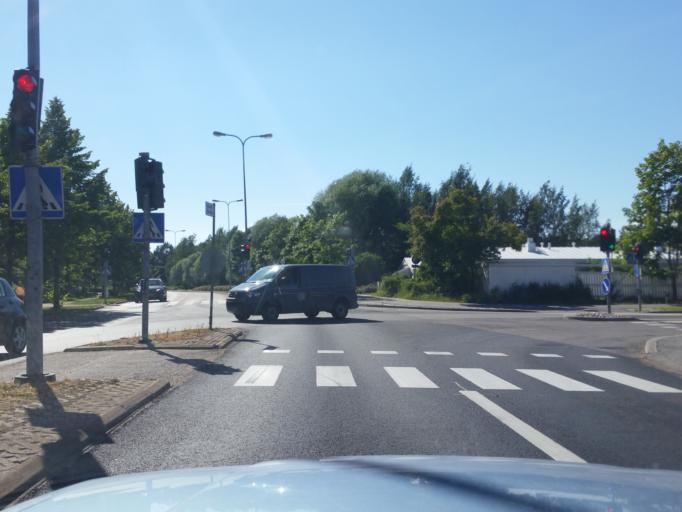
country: FI
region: Uusimaa
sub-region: Helsinki
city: Otaniemi
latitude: 60.1847
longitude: 24.8035
